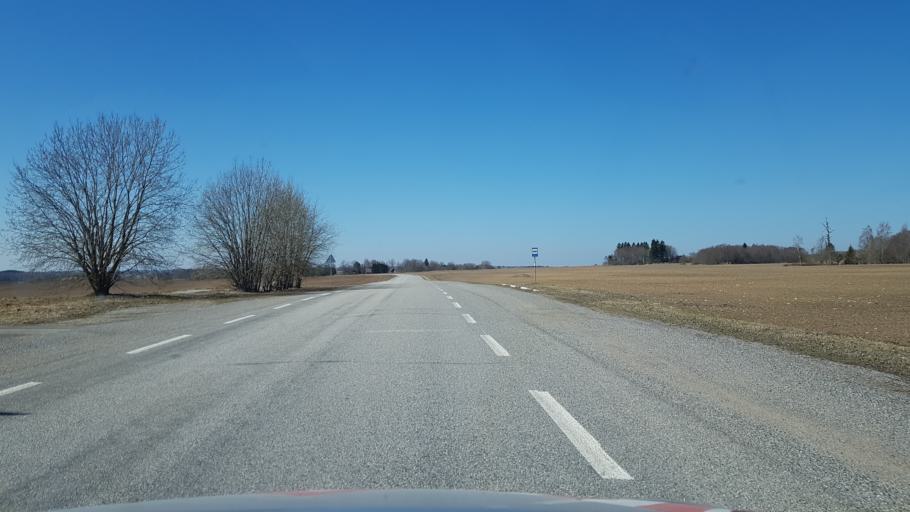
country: EE
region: Laeaene-Virumaa
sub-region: Vinni vald
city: Vinni
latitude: 59.0694
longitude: 26.5251
